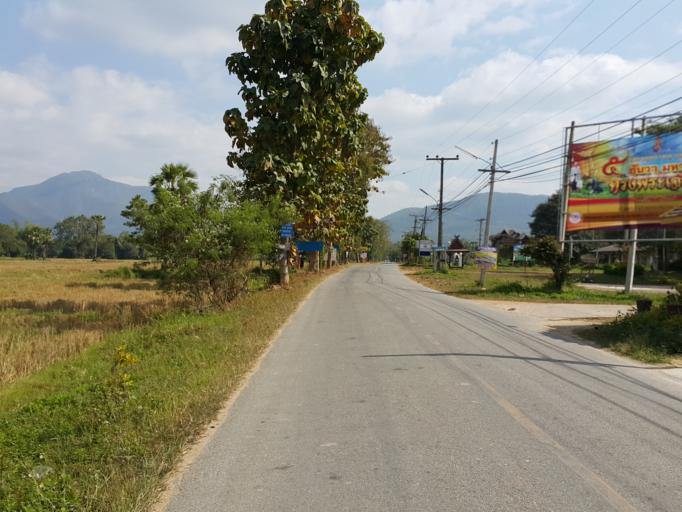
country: TH
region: Chiang Mai
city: Mae On
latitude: 18.7248
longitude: 99.2013
